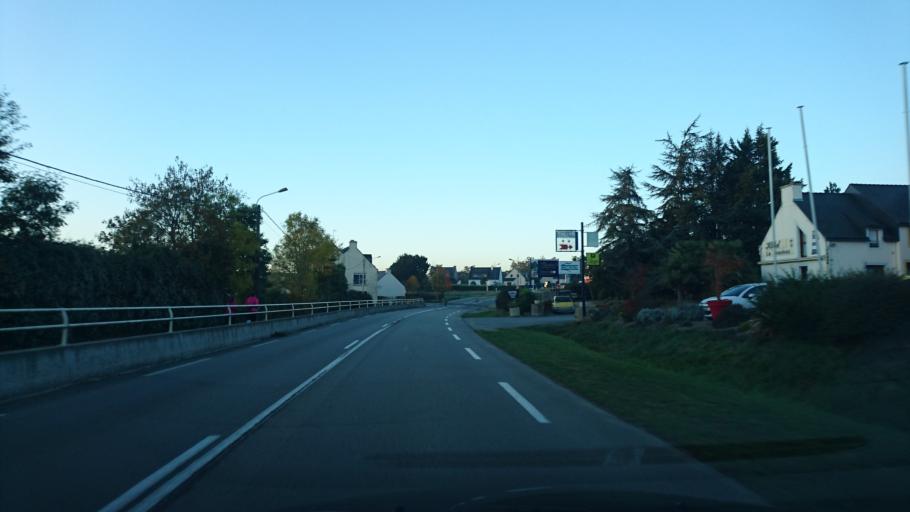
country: FR
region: Brittany
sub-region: Departement du Morbihan
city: Pluneret
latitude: 47.6645
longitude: -2.9670
